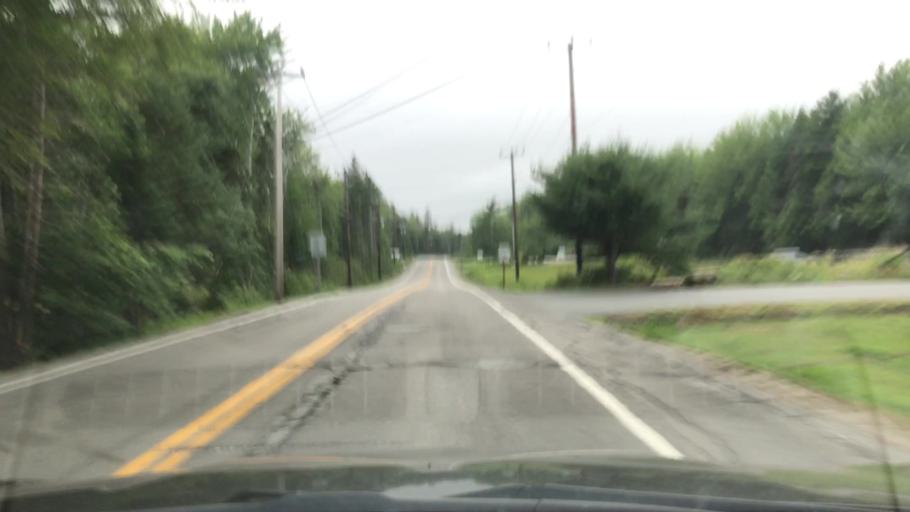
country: US
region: Maine
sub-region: Hancock County
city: Trenton
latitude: 44.4071
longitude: -68.3484
